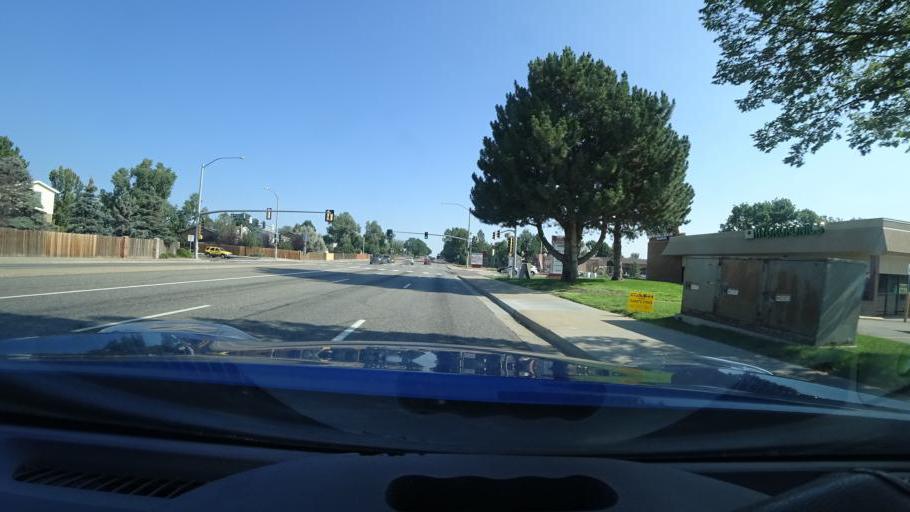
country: US
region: Colorado
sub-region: Adams County
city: Aurora
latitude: 39.6851
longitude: -104.8098
